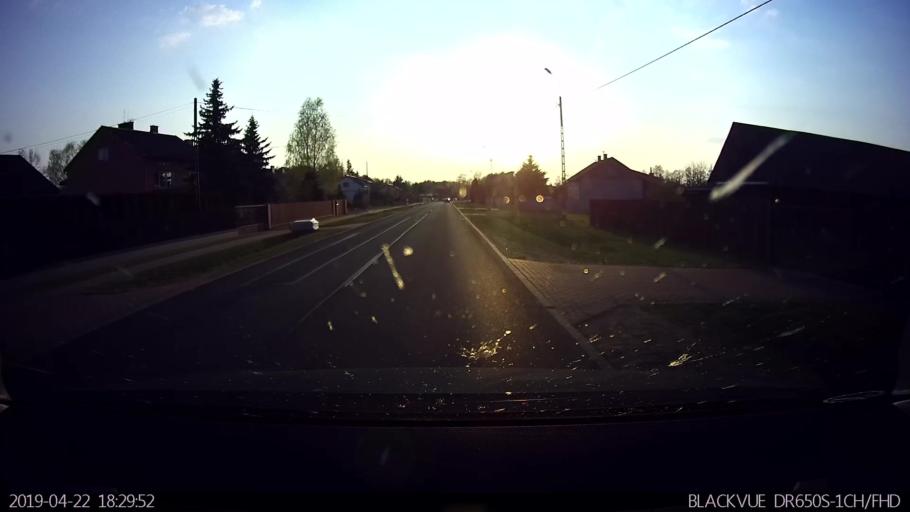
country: PL
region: Masovian Voivodeship
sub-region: Powiat wolominski
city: Tluszcz
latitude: 52.4519
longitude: 21.4442
